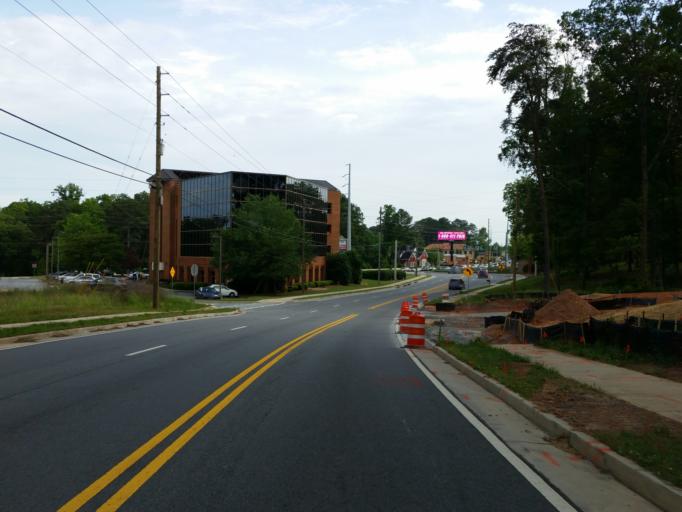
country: US
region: Georgia
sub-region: Cobb County
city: Marietta
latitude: 33.9754
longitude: -84.4852
